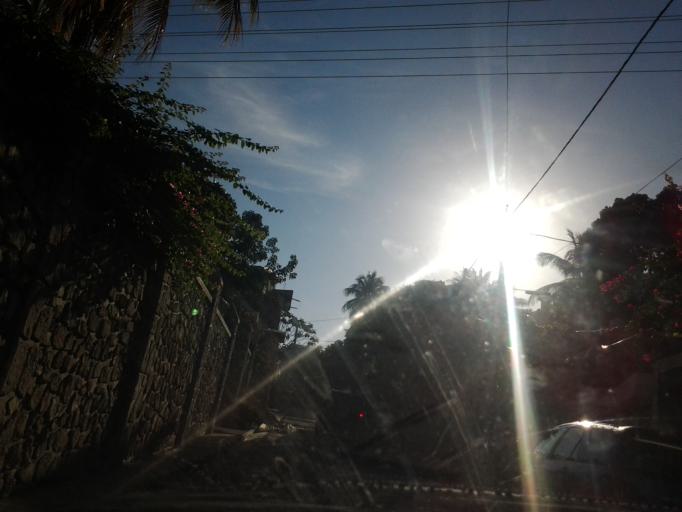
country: HT
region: Ouest
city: Delmas 73
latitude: 18.5451
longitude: -72.3184
